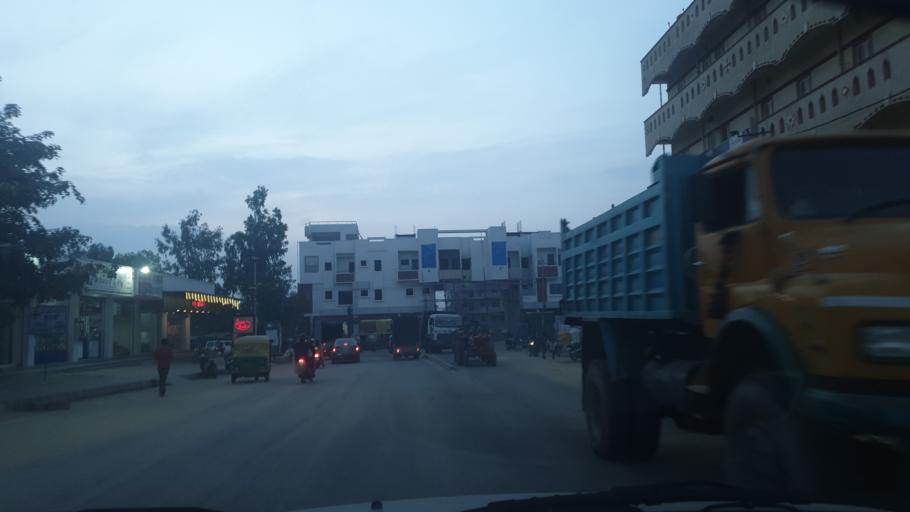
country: IN
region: Karnataka
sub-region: Bangalore Urban
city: Yelahanka
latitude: 13.0401
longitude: 77.6782
